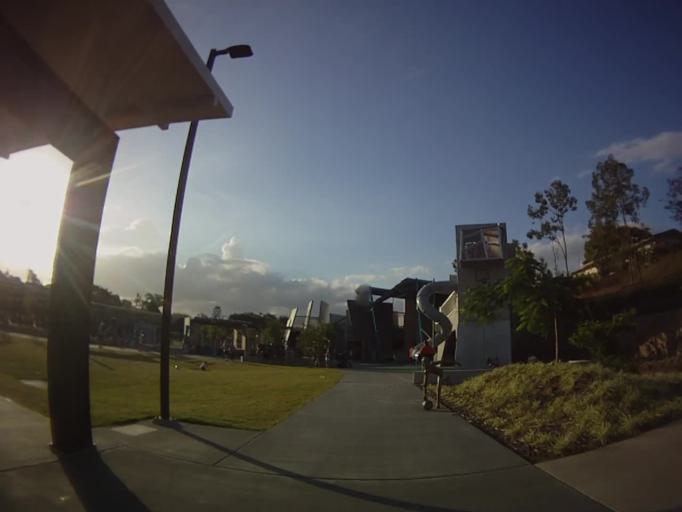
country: AU
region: Queensland
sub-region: Brisbane
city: Milton
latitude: -27.4695
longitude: 153.0009
